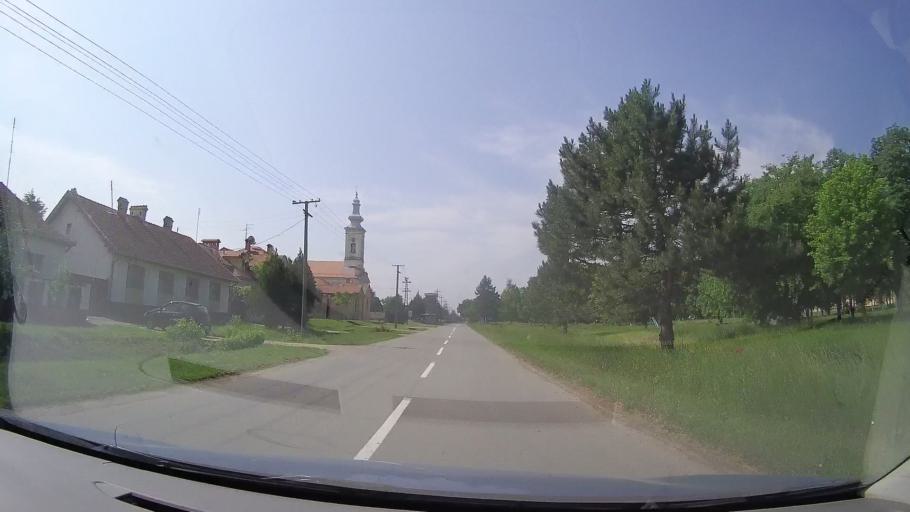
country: RS
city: Samos
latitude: 45.2034
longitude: 20.7732
